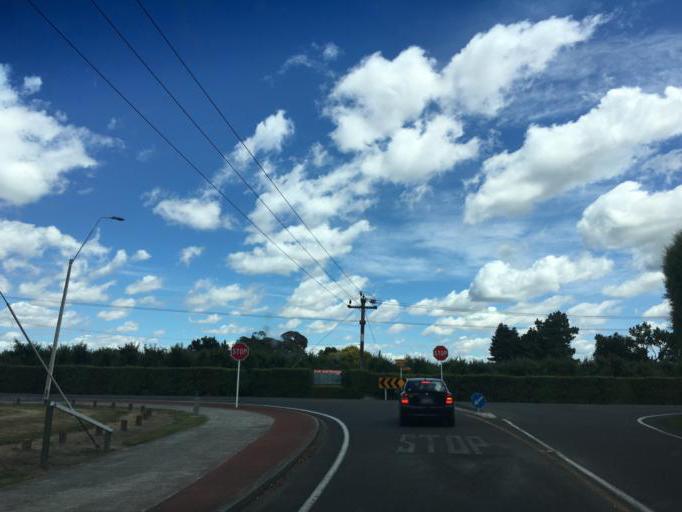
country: NZ
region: Hawke's Bay
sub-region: Hastings District
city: Hastings
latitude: -39.6532
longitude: 176.8759
